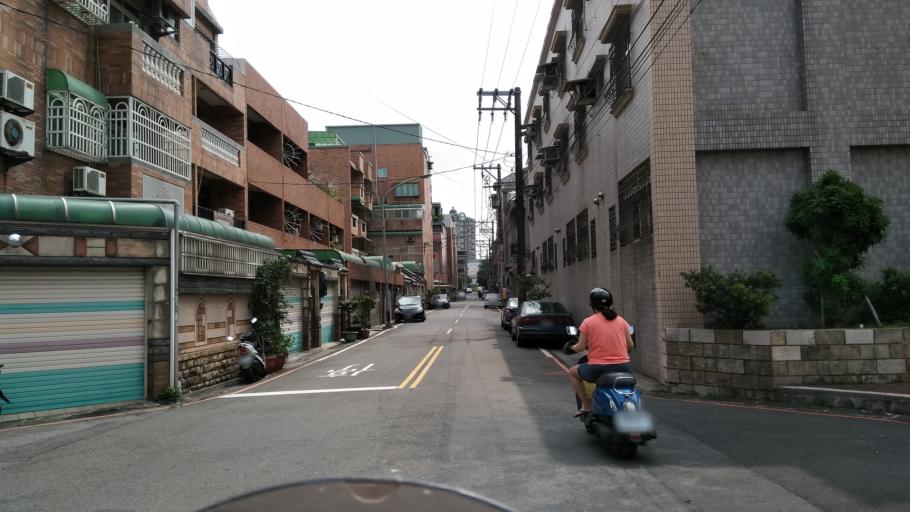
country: TW
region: Taiwan
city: Taoyuan City
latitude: 25.0210
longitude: 121.2654
